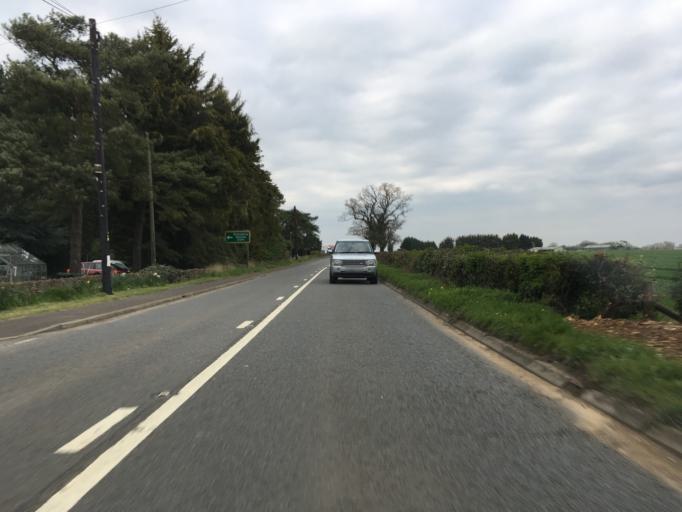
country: GB
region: England
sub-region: Wiltshire
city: Hankerton
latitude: 51.6608
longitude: -2.0523
